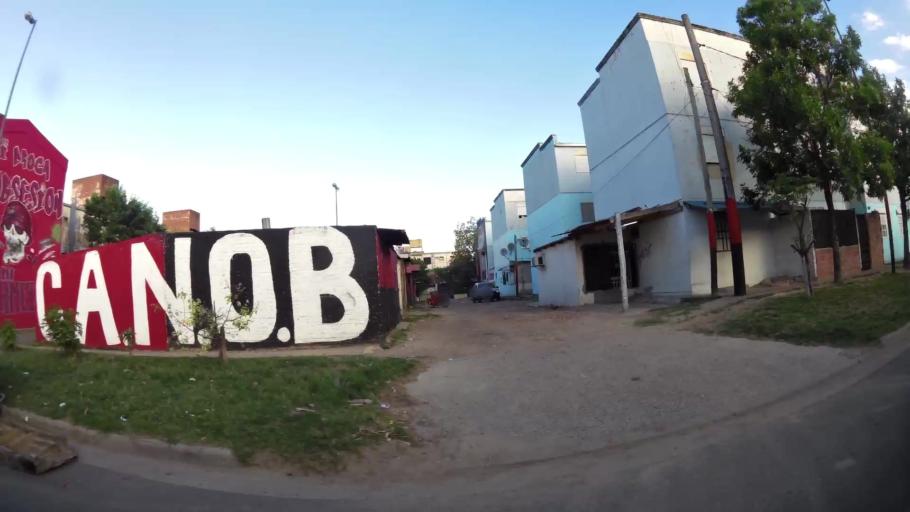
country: AR
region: Santa Fe
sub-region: Departamento de Rosario
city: Rosario
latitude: -32.9793
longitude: -60.6694
